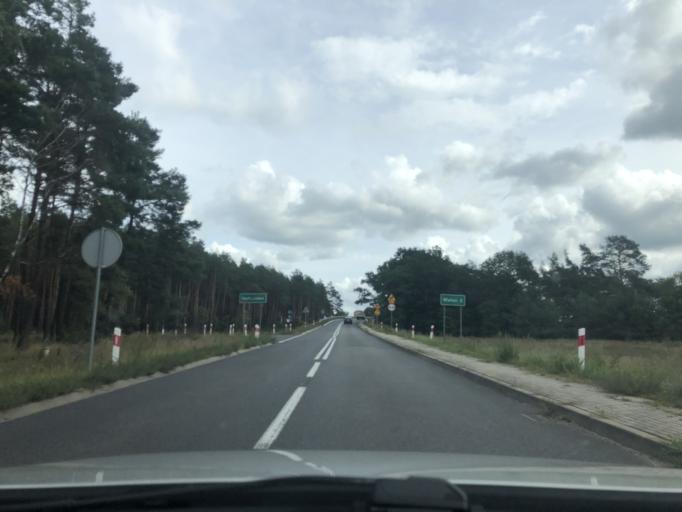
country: PL
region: Greater Poland Voivodeship
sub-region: Powiat czarnkowsko-trzcianecki
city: Wielen
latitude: 52.9029
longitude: 16.1132
